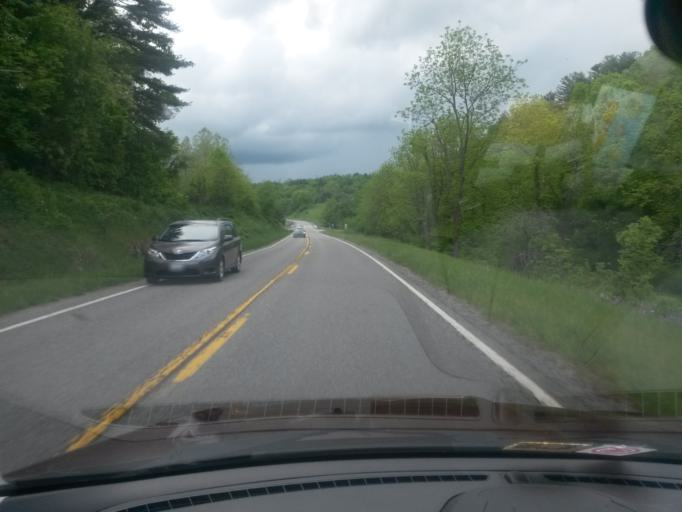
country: US
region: Virginia
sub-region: Floyd County
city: Floyd
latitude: 36.9369
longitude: -80.3379
